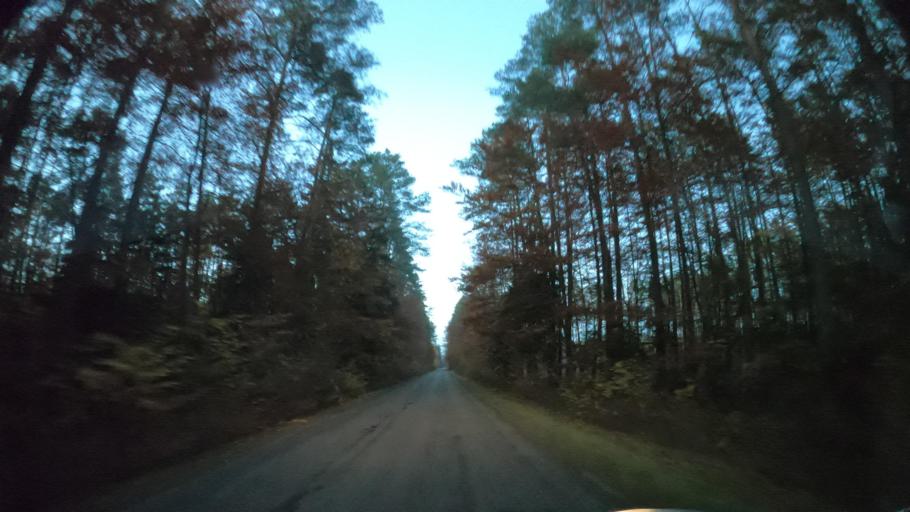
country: PL
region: Greater Poland Voivodeship
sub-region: Powiat zlotowski
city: Sypniewo
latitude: 53.4157
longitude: 16.5901
